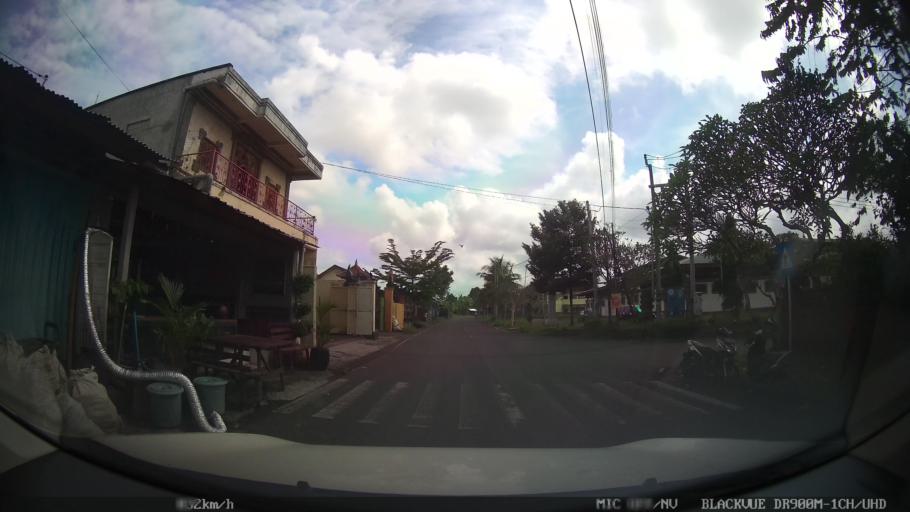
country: ID
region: Bali
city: Banjar Tebongkang
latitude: -8.5316
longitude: 115.2512
